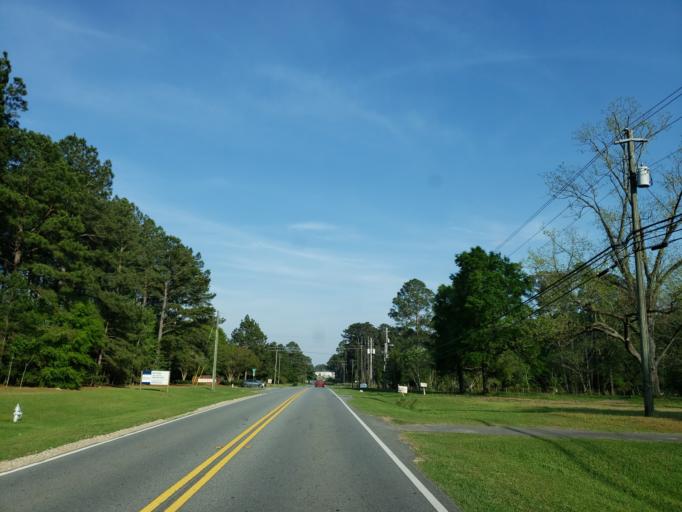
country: US
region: Georgia
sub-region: Tift County
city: Tifton
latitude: 31.4654
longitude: -83.5394
